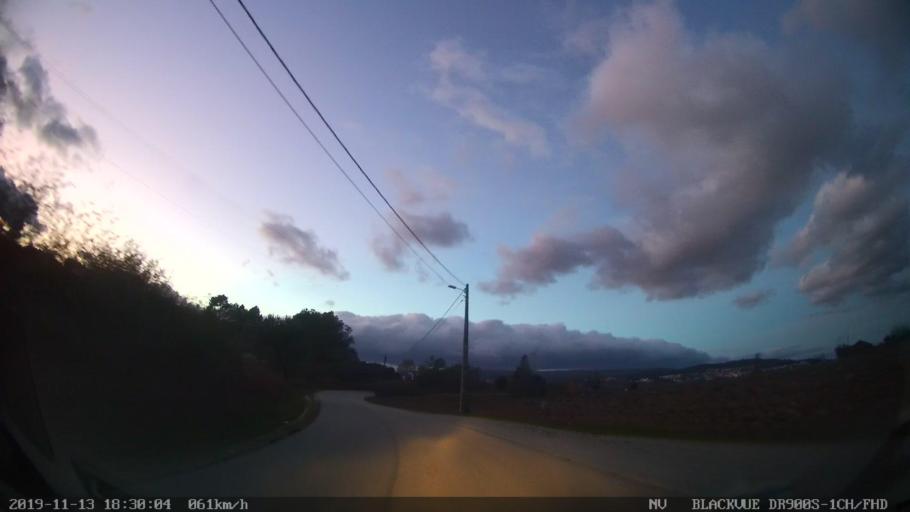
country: PT
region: Vila Real
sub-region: Sabrosa
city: Sabrosa
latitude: 41.2434
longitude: -7.5711
